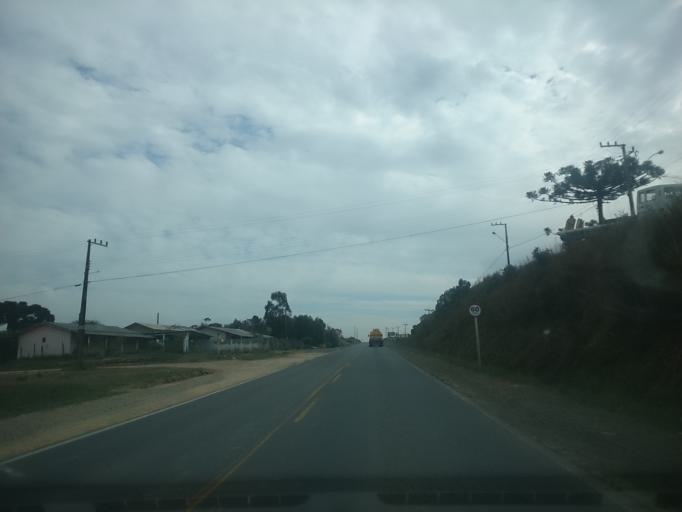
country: BR
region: Santa Catarina
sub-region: Lages
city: Lages
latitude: -27.7741
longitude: -50.3199
